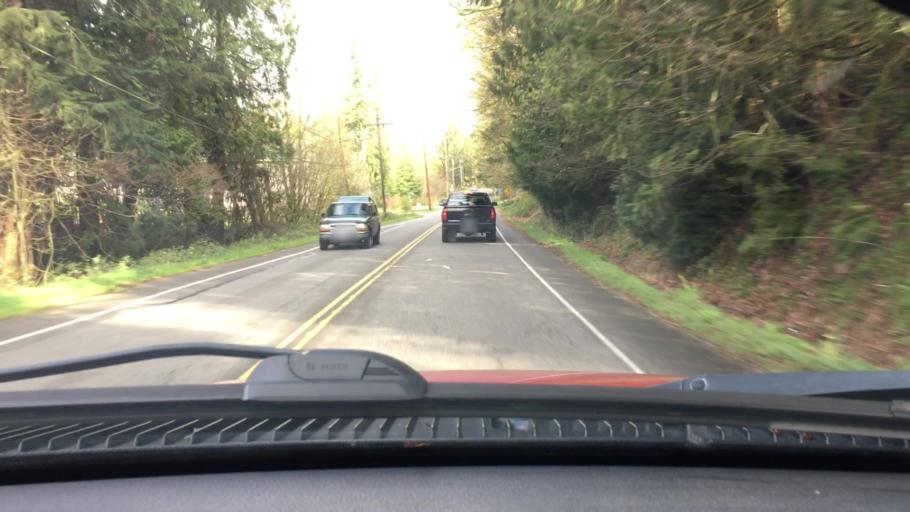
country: US
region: Washington
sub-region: King County
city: Maple Valley
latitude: 47.3725
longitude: -122.0474
